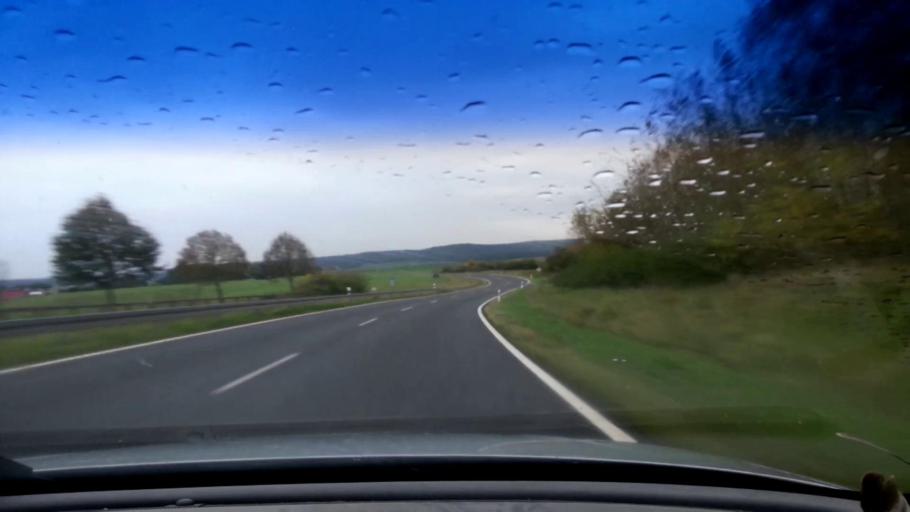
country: DE
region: Bavaria
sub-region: Upper Franconia
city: Priesendorf
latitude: 49.8658
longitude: 10.7177
